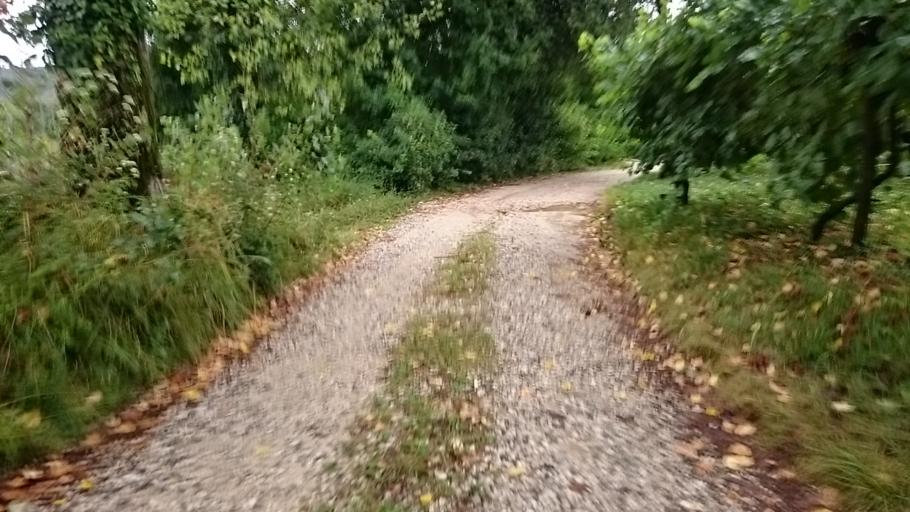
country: IT
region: Veneto
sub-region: Provincia di Treviso
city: Monfumo
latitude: 45.8213
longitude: 11.9175
